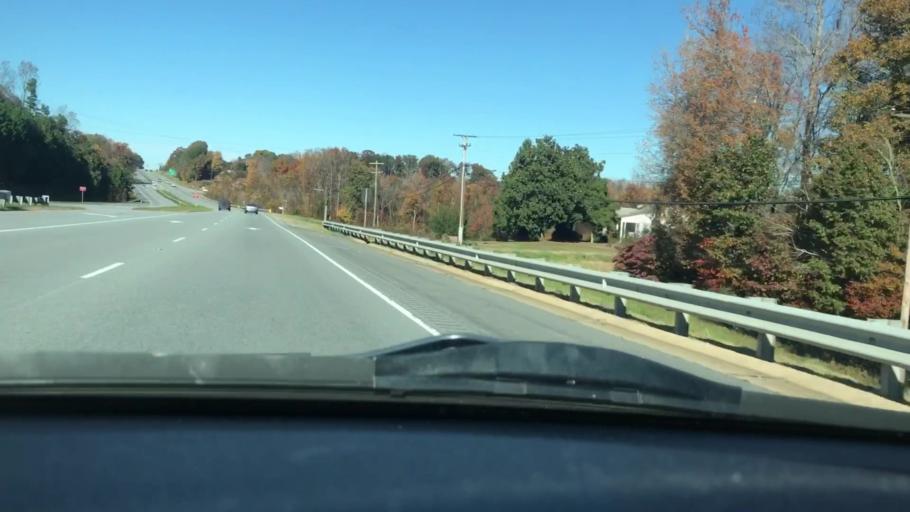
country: US
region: North Carolina
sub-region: Rockingham County
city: Madison
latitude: 36.3603
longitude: -79.9452
